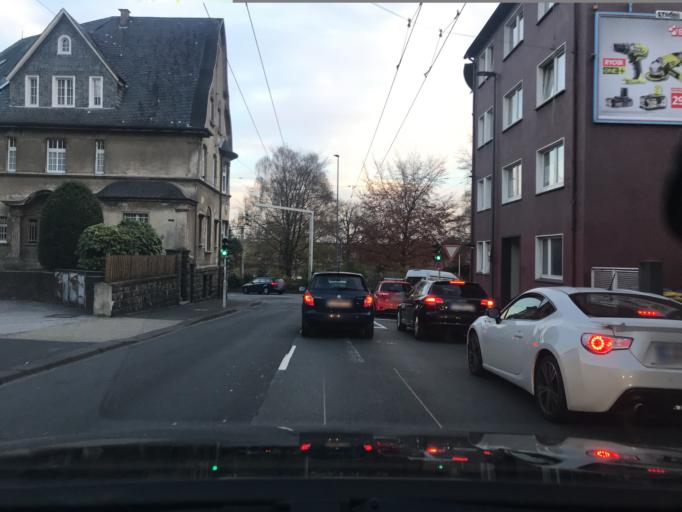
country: DE
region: North Rhine-Westphalia
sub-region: Regierungsbezirk Dusseldorf
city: Solingen
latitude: 51.1675
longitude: 7.0792
